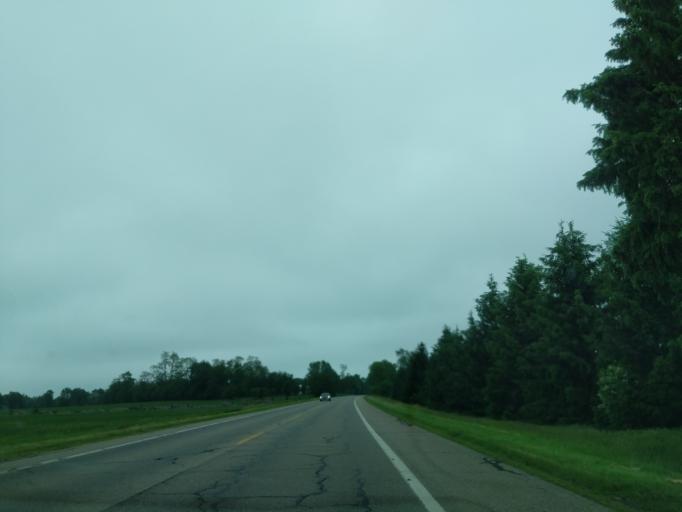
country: US
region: Michigan
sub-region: Hillsdale County
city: Jonesville
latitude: 42.0249
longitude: -84.7018
